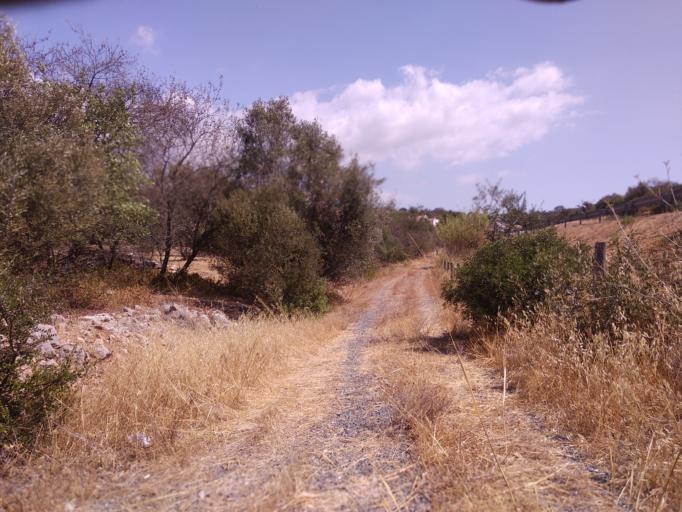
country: PT
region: Faro
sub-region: Sao Bras de Alportel
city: Sao Bras de Alportel
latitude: 37.1481
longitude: -7.8872
